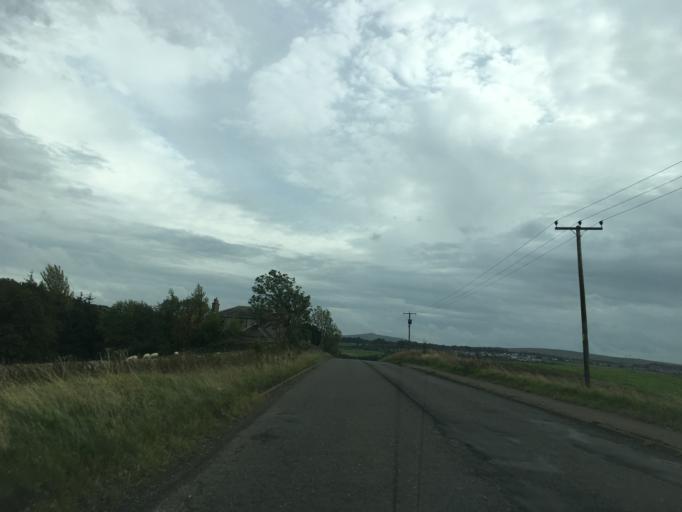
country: GB
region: Scotland
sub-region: West Lothian
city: Kirknewton
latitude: 55.9079
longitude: -3.4070
